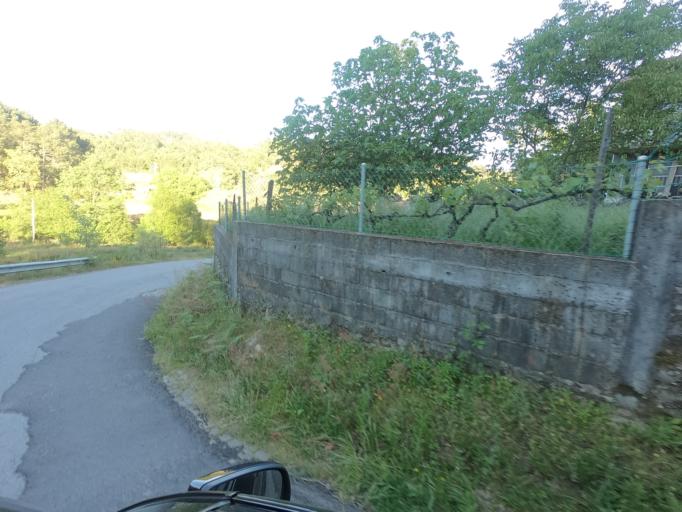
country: PT
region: Vila Real
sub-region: Vila Real
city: Vila Real
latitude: 41.3385
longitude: -7.7345
